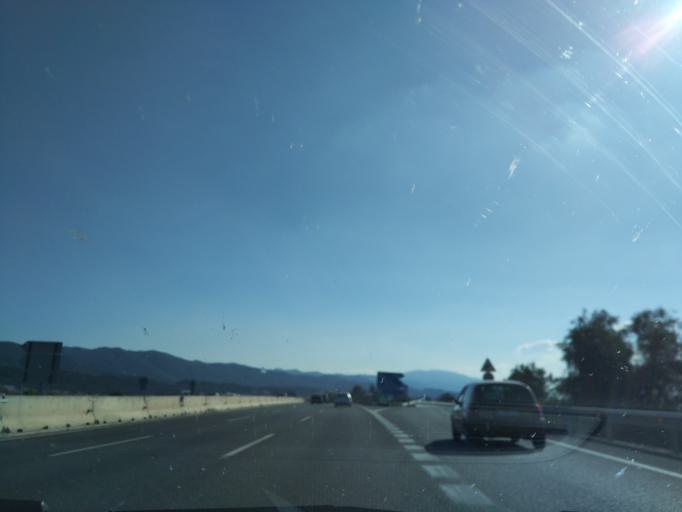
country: ES
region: Murcia
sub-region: Murcia
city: Murcia
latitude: 37.9491
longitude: -1.1452
